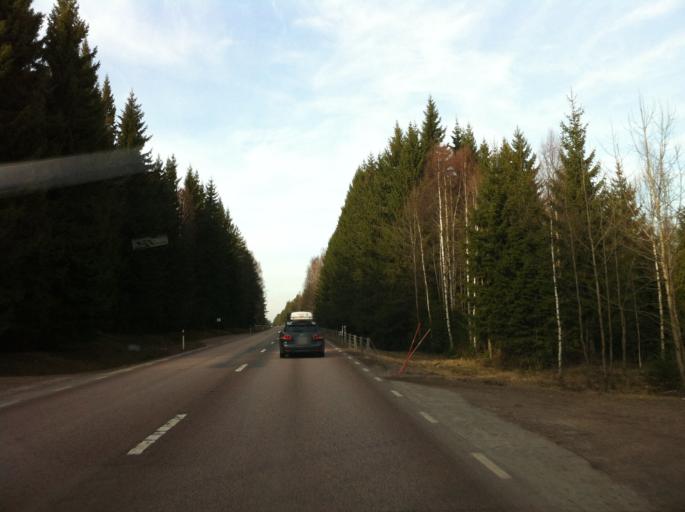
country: SE
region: Vaermland
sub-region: Kristinehamns Kommun
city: Bjorneborg
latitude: 59.2206
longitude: 14.1840
